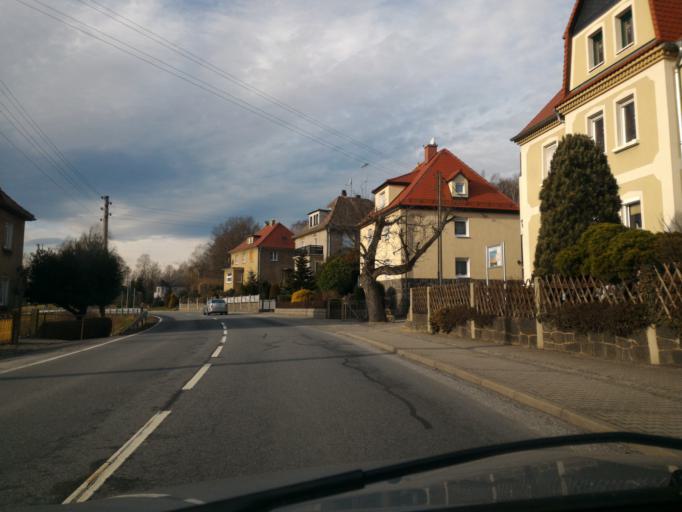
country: DE
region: Saxony
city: Demitz-Thumitz
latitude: 51.0997
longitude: 14.2399
